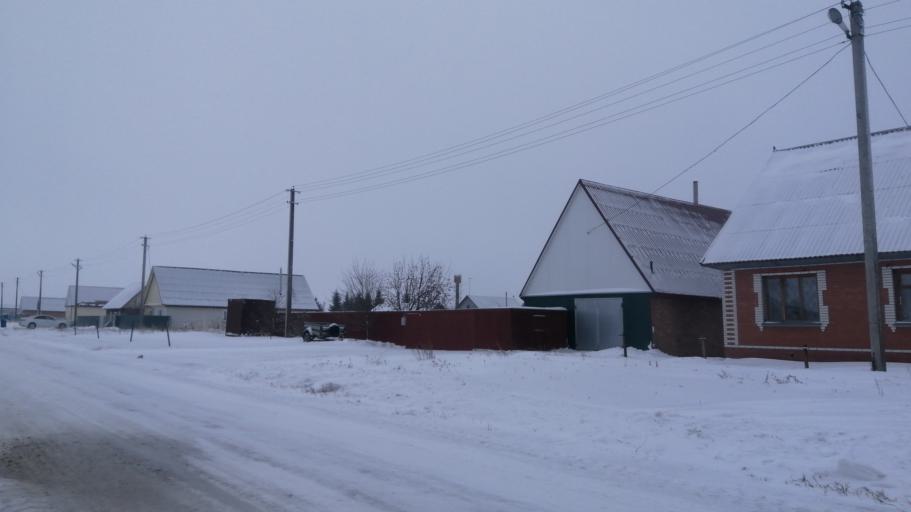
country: RU
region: Novosibirsk
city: Krasnozerskoye
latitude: 53.9929
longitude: 79.2632
